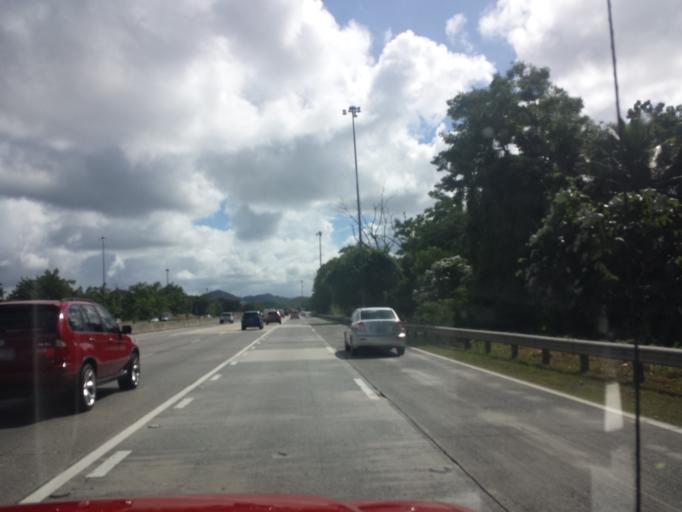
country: PR
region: Guaynabo
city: Guaynabo
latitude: 18.3648
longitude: -66.0704
